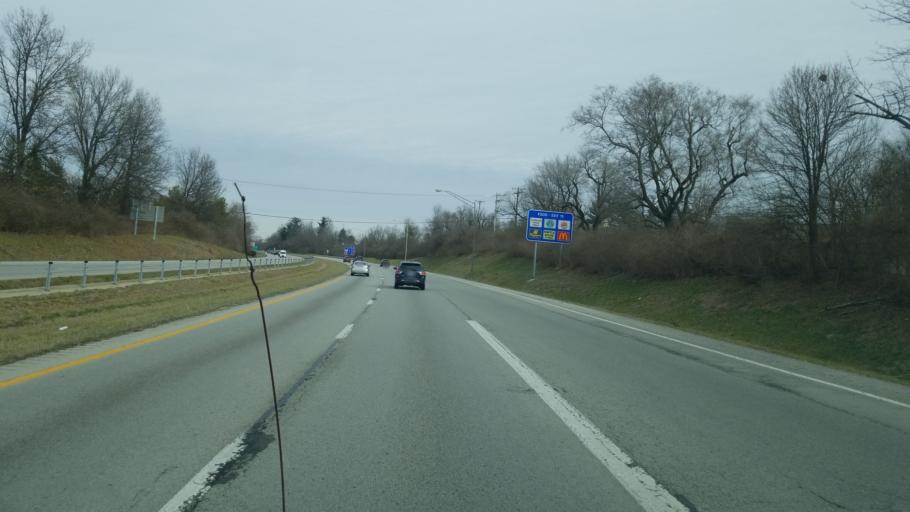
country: US
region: Kentucky
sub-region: Fayette County
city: Lexington
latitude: 37.9976
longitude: -84.4637
